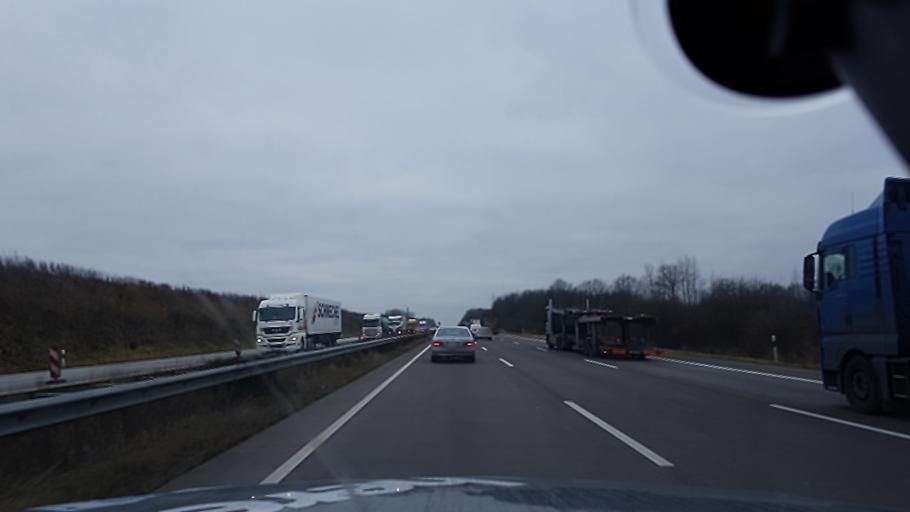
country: DE
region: Schleswig-Holstein
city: Hoisdorf
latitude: 53.6735
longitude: 10.3083
